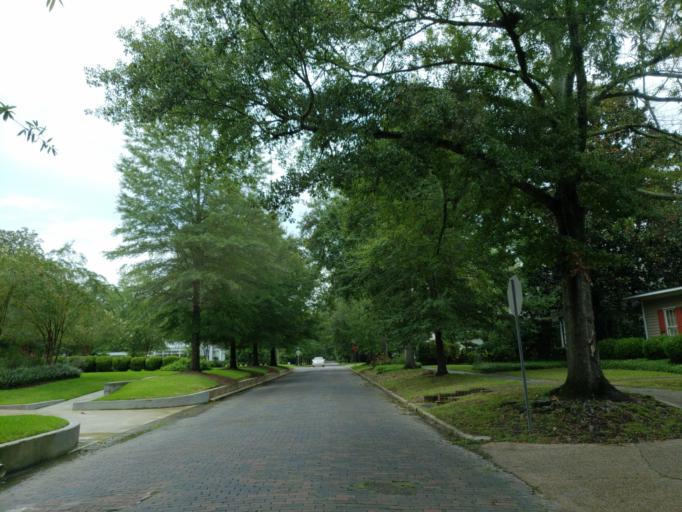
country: US
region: Mississippi
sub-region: Forrest County
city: Hattiesburg
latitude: 31.3203
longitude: -89.3011
